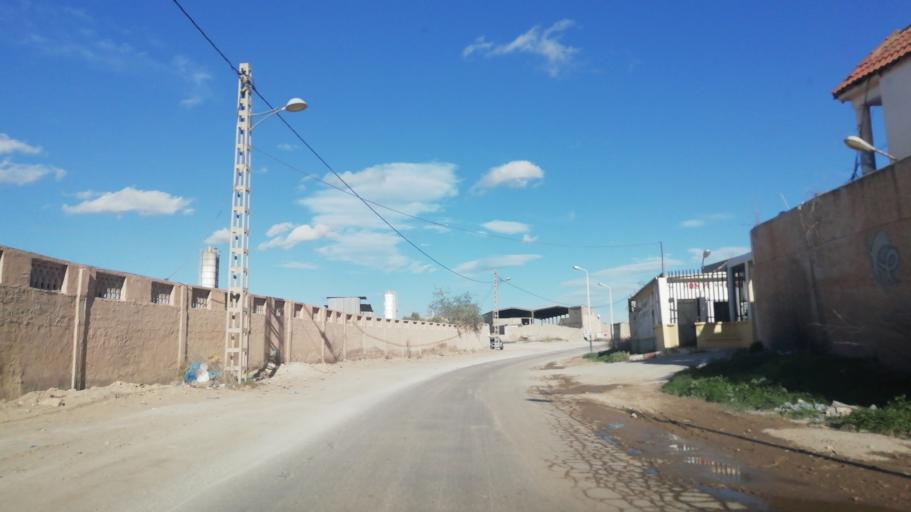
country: DZ
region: Oran
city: Sidi ech Chahmi
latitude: 35.6397
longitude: -0.5458
